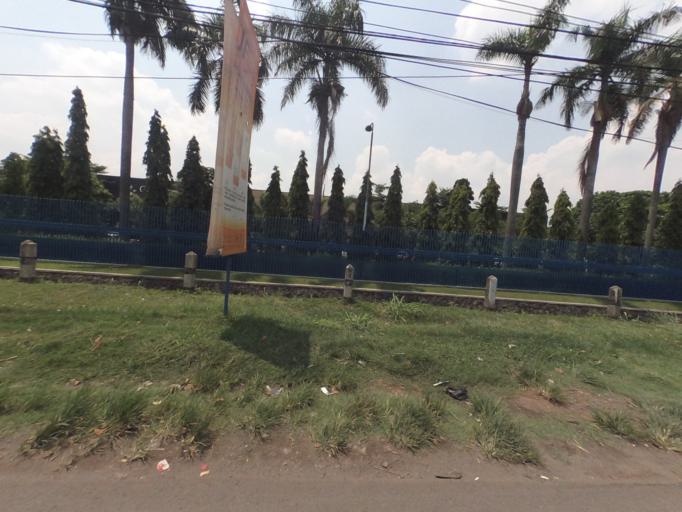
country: ID
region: West Java
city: Cibinong
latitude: -6.5402
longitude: 106.8264
